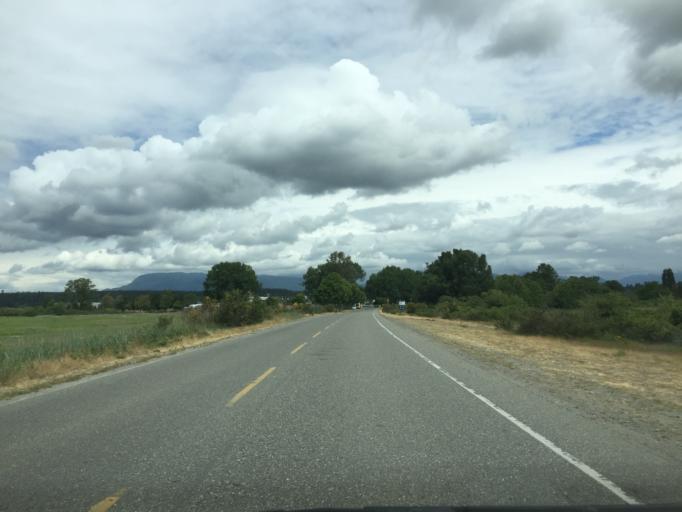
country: CA
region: British Columbia
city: Richmond
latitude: 49.2131
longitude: -123.2023
